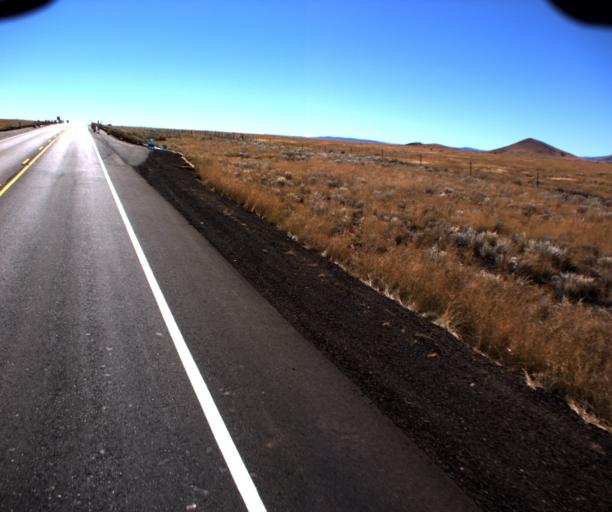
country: US
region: Arizona
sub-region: Apache County
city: Springerville
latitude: 34.2752
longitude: -109.3639
